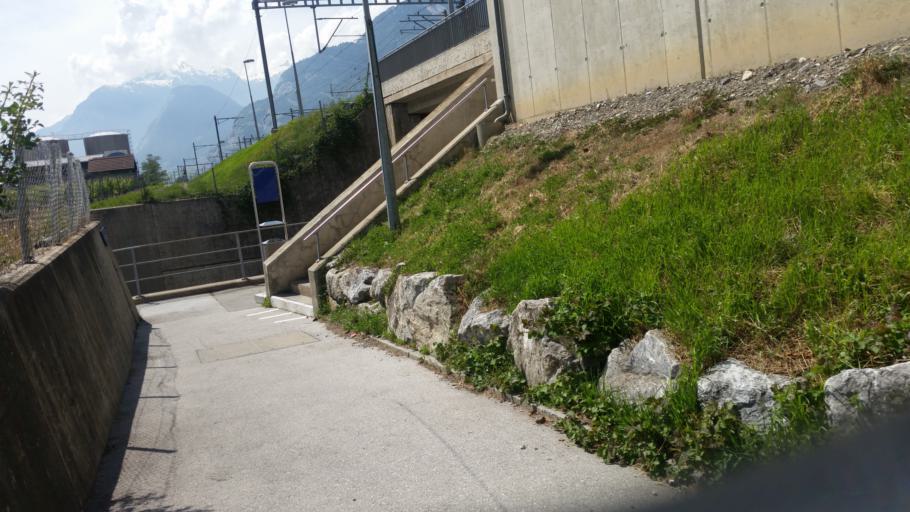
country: CH
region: Valais
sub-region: Conthey District
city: Conthey
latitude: 46.2158
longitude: 7.3048
